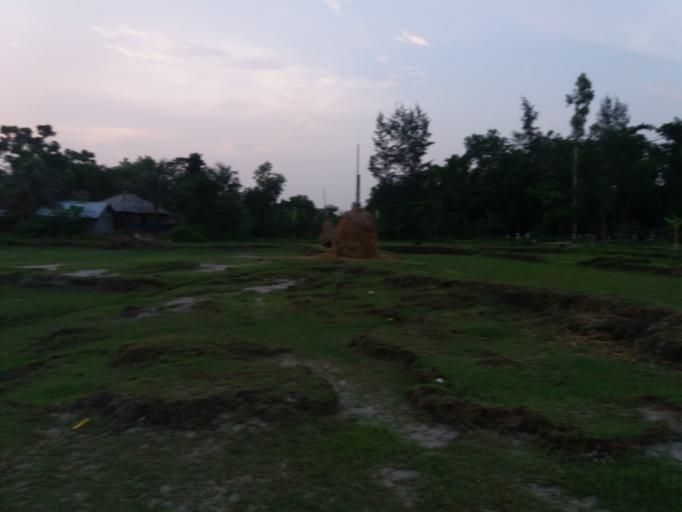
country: BD
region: Chittagong
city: Feni
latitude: 22.9342
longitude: 91.3464
